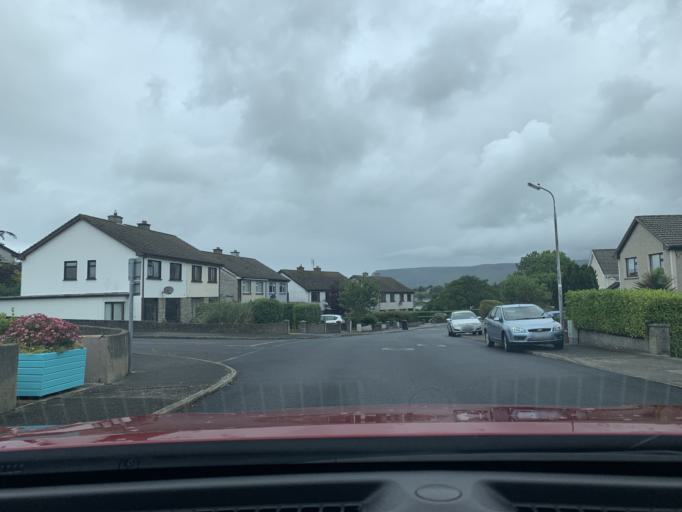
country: IE
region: Connaught
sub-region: Sligo
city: Sligo
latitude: 54.2807
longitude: -8.4818
